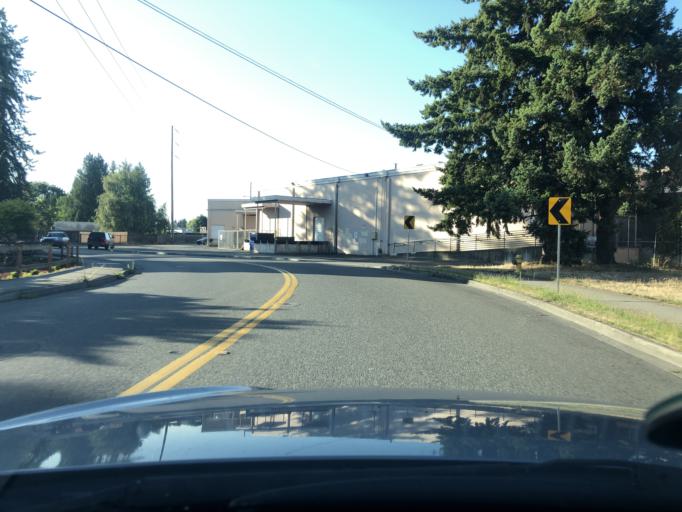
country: US
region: Washington
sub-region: King County
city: Auburn
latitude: 47.2918
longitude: -122.2129
